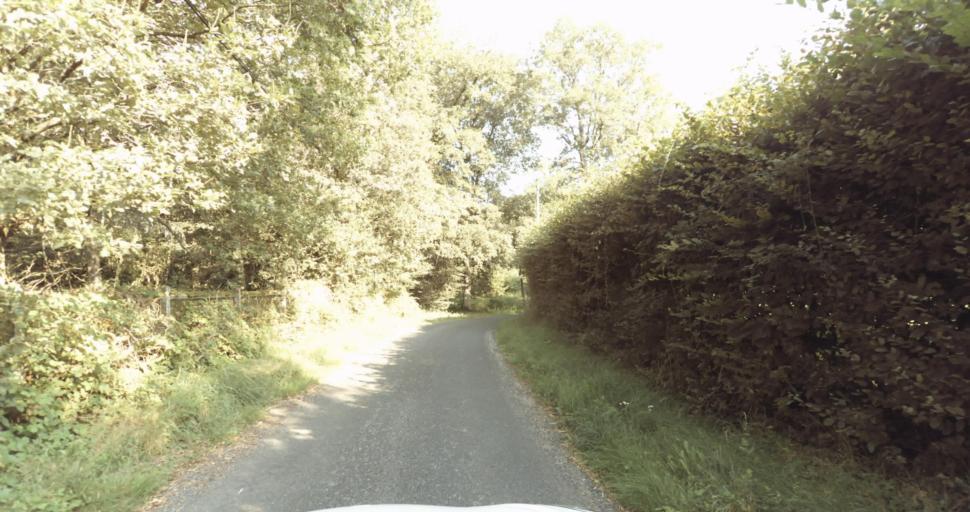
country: FR
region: Haute-Normandie
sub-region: Departement de l'Eure
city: Tillieres-sur-Avre
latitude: 48.7999
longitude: 1.1105
